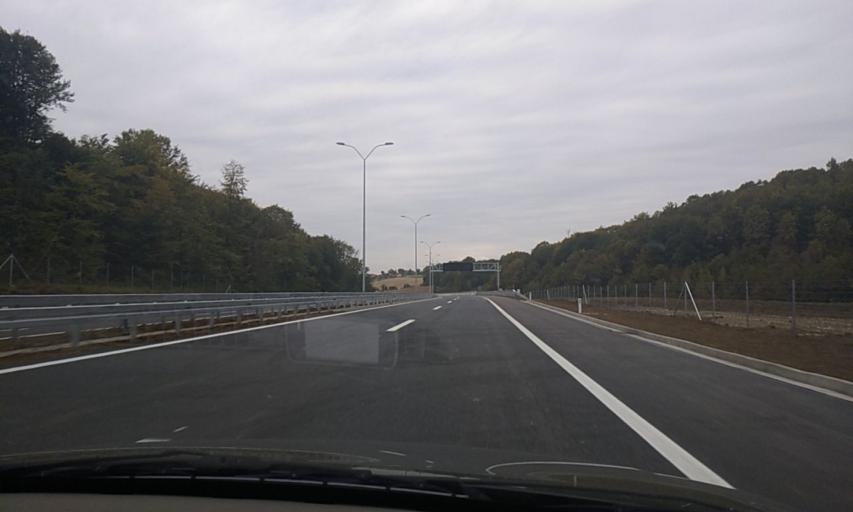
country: BA
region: Republika Srpska
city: Prnjavor
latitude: 44.8691
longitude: 17.5079
